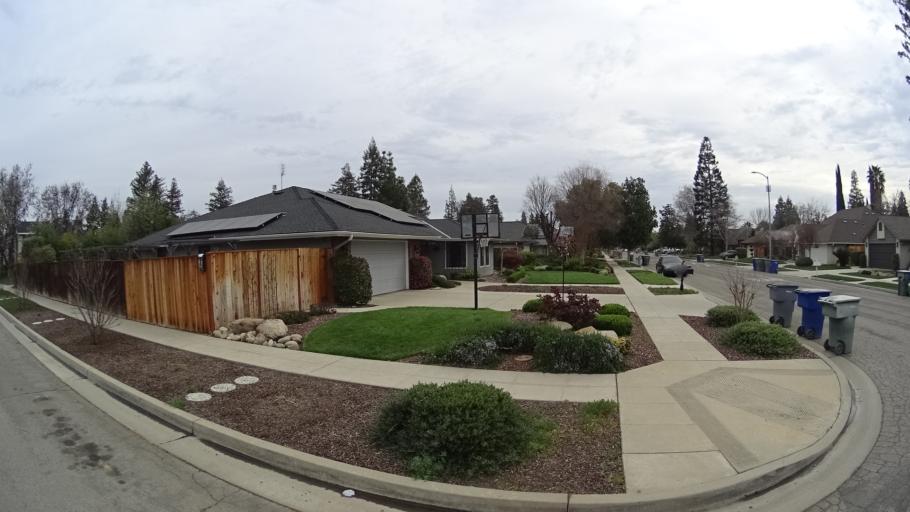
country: US
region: California
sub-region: Fresno County
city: Clovis
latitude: 36.8470
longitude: -119.7608
